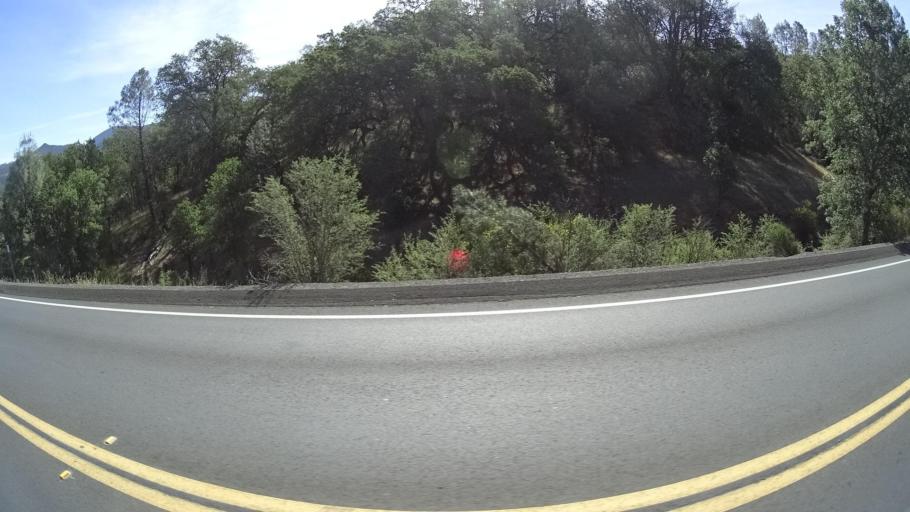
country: US
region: California
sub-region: Lake County
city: Kelseyville
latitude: 38.9590
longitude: -122.8274
